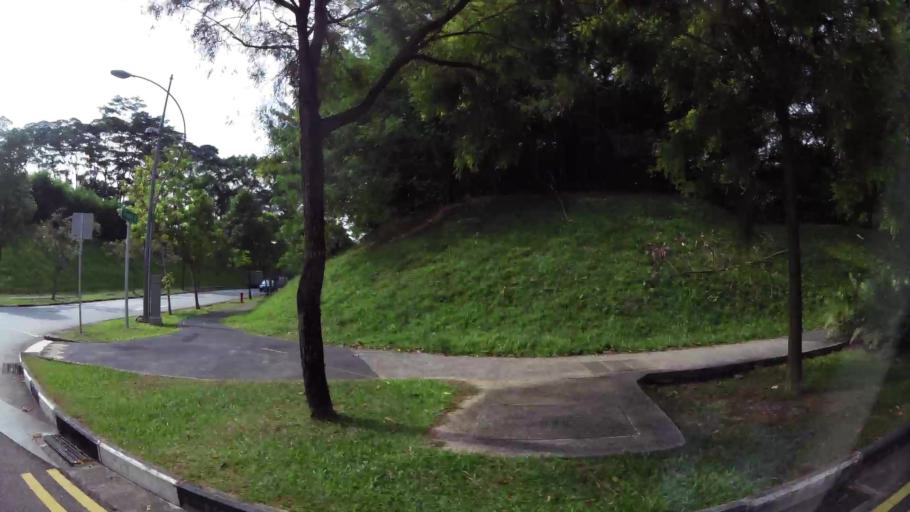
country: SG
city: Singapore
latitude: 1.3011
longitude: 103.7916
